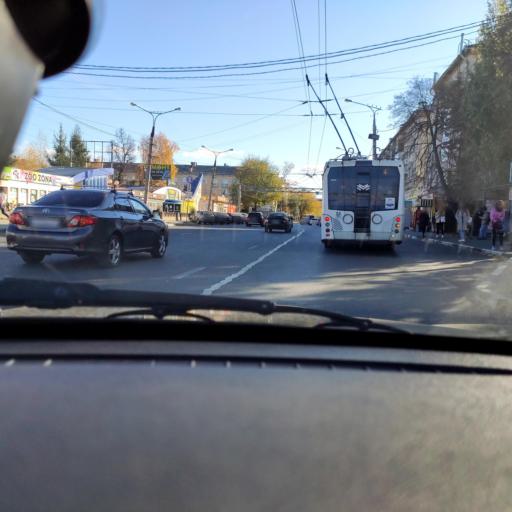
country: RU
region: Samara
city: Tol'yatti
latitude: 53.5096
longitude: 49.4153
